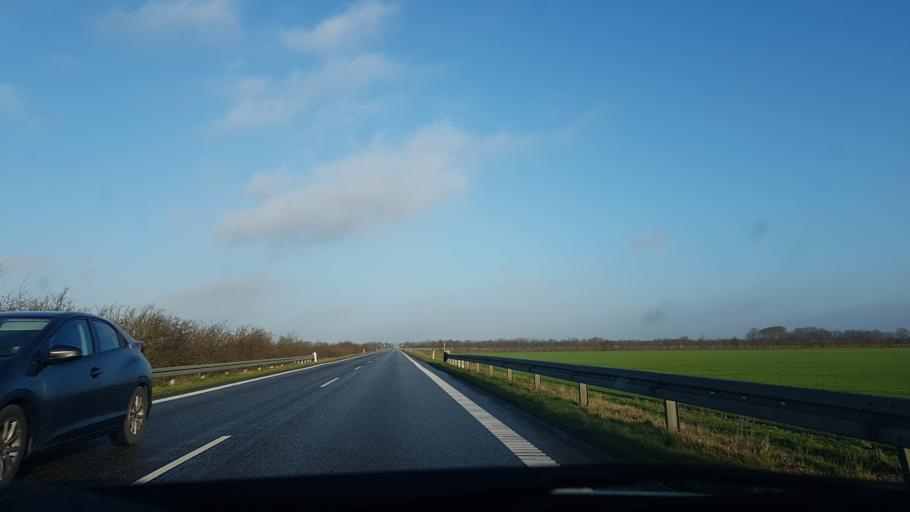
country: DK
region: South Denmark
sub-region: Tonder Kommune
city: Toftlund
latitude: 55.2183
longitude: 9.1047
